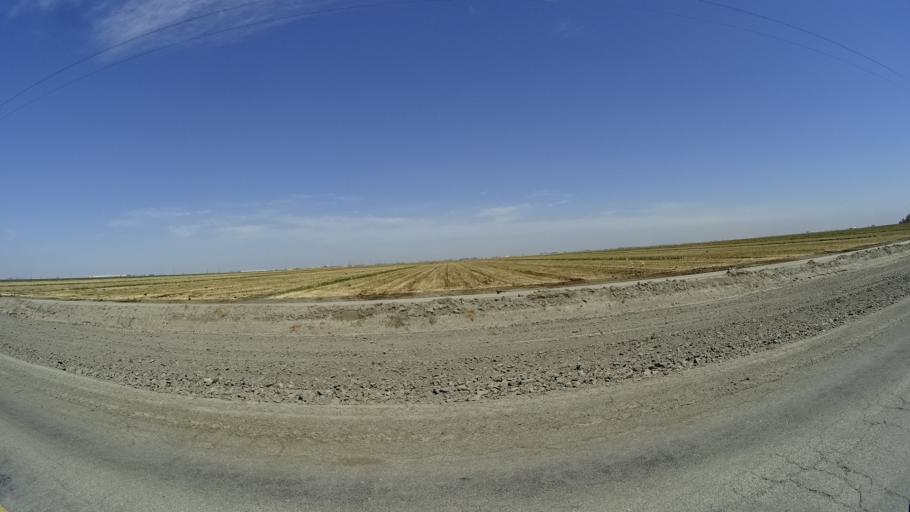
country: US
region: California
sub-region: Kings County
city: Corcoran
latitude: 36.1379
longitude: -119.6616
